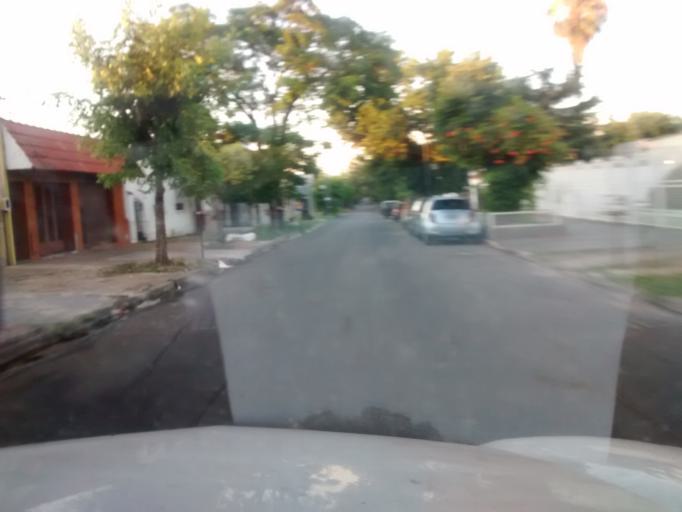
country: AR
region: Buenos Aires
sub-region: Partido de La Plata
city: La Plata
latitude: -34.9429
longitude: -57.9491
